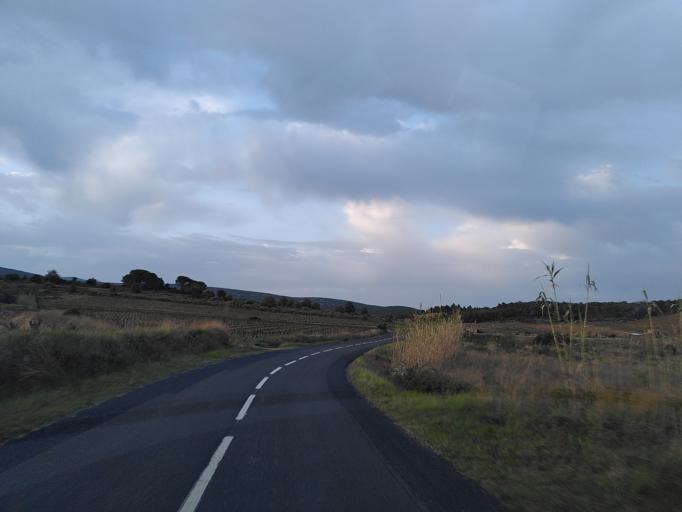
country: FR
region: Languedoc-Roussillon
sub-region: Departement des Pyrenees-Orientales
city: Estagel
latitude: 42.8071
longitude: 2.6986
